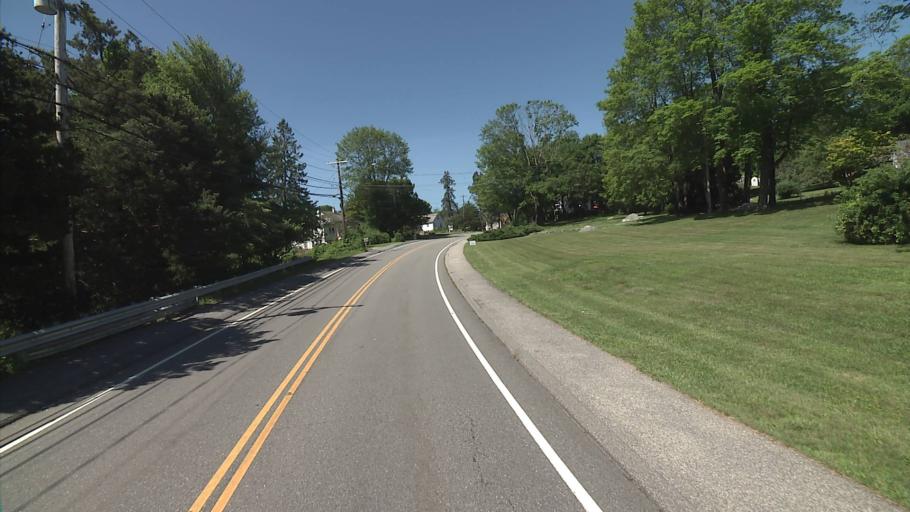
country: US
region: Connecticut
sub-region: New London County
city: Noank
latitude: 41.3415
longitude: -71.9829
